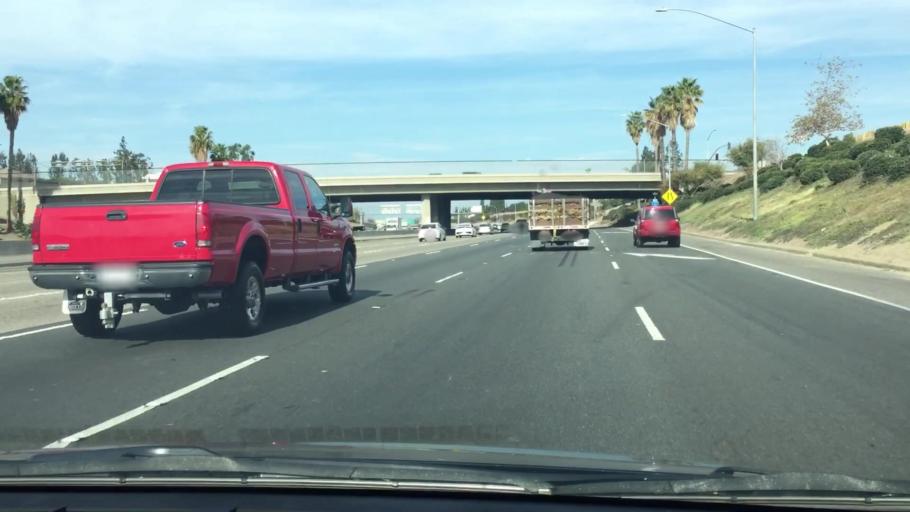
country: US
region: California
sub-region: Orange County
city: Tustin
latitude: 33.7471
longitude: -117.8324
